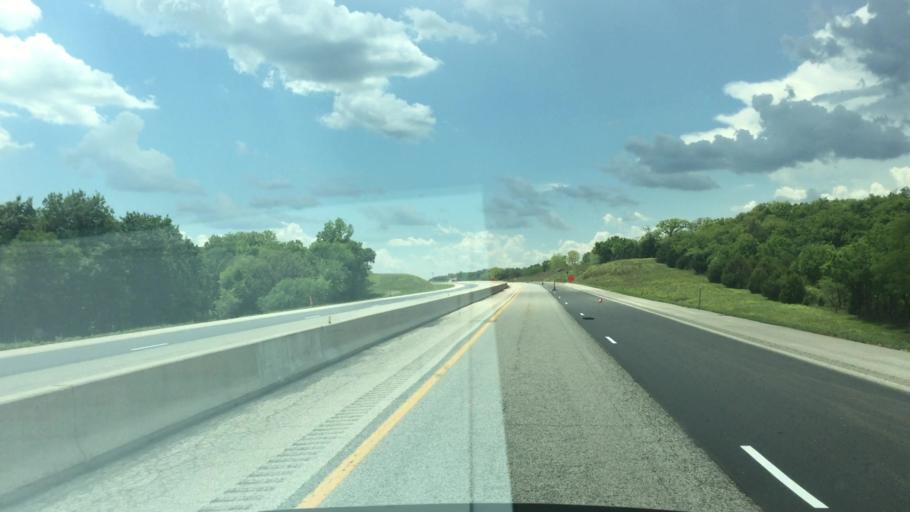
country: US
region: Kansas
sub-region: Shawnee County
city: Auburn
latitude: 38.8919
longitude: -95.8093
